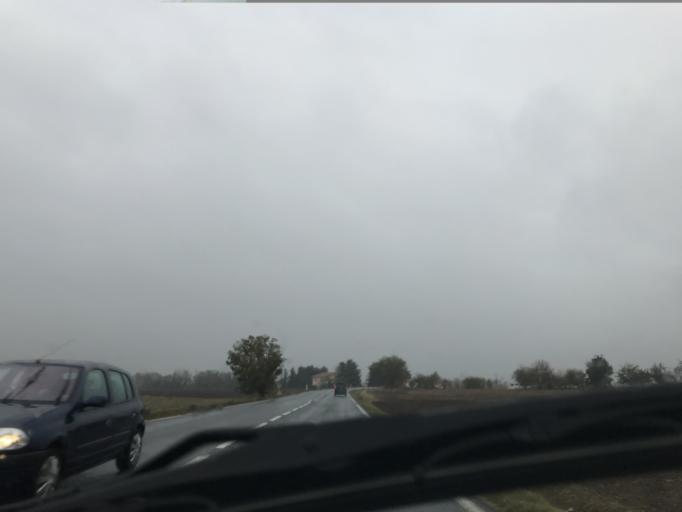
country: FR
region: Auvergne
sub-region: Departement du Puy-de-Dome
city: Dallet
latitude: 45.7828
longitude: 3.2485
